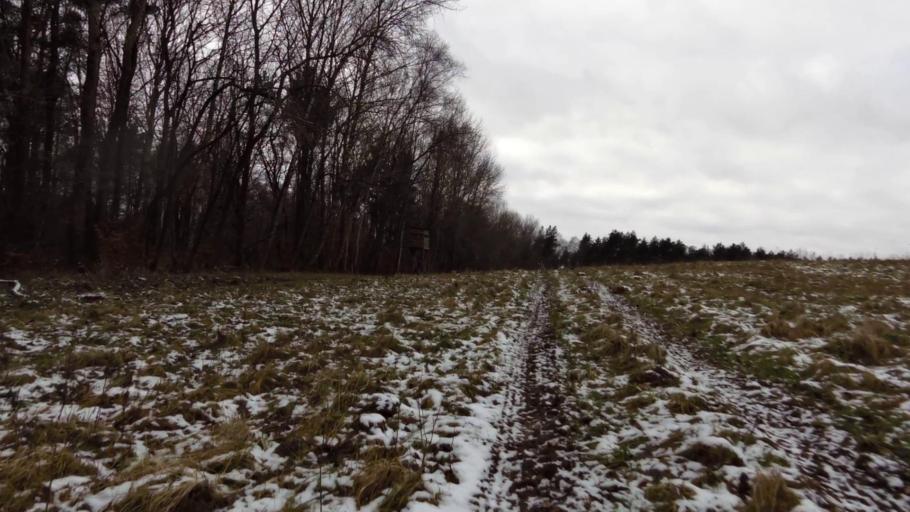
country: PL
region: West Pomeranian Voivodeship
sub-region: Powiat drawski
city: Drawsko Pomorskie
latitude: 53.5420
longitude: 15.7092
